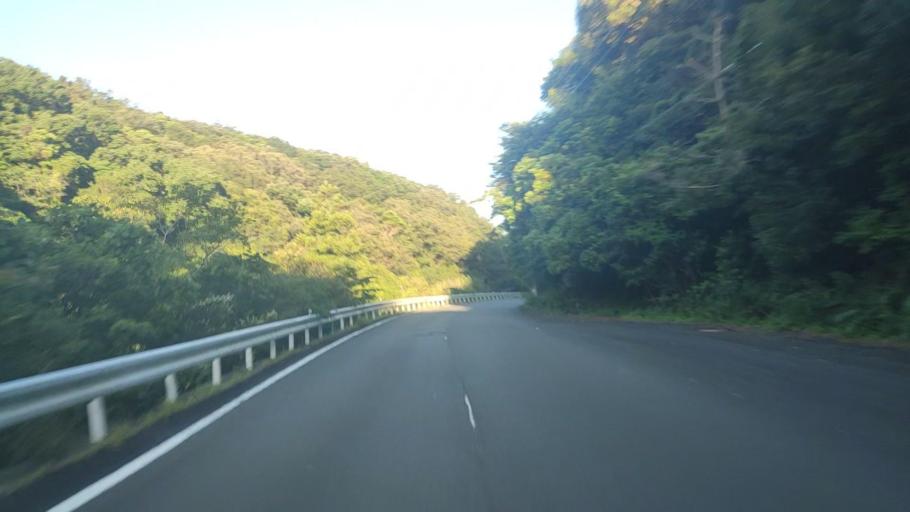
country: JP
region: Mie
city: Toba
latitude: 34.2633
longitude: 136.7733
